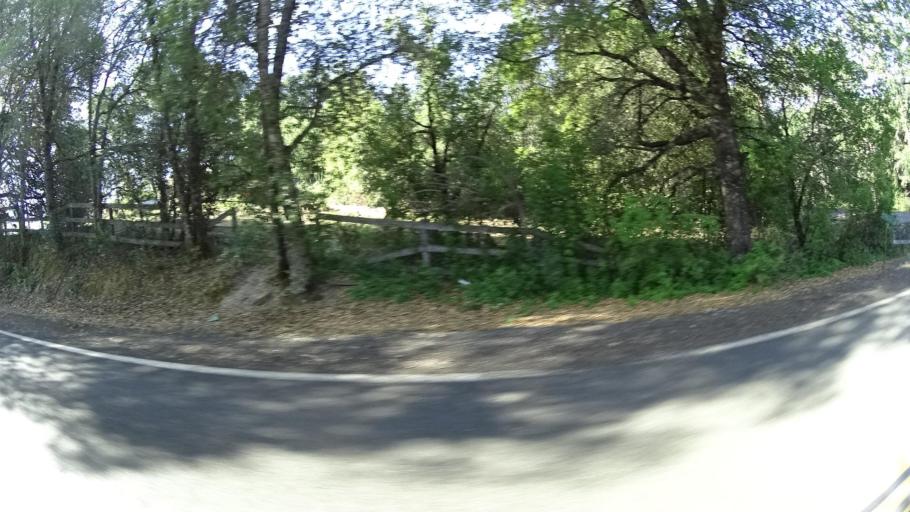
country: US
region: California
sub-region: Lake County
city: Lakeport
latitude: 39.0405
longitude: -122.9399
